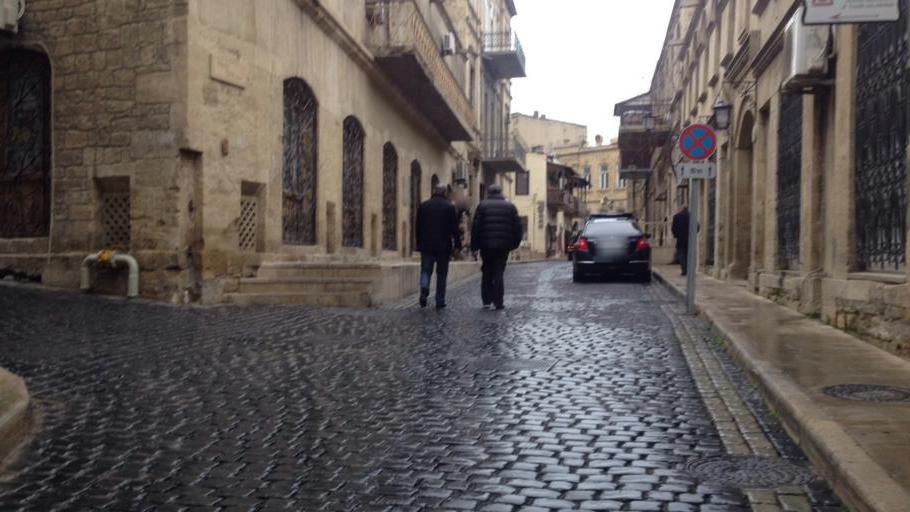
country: AZ
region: Baki
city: Badamdar
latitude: 40.3658
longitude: 49.8355
